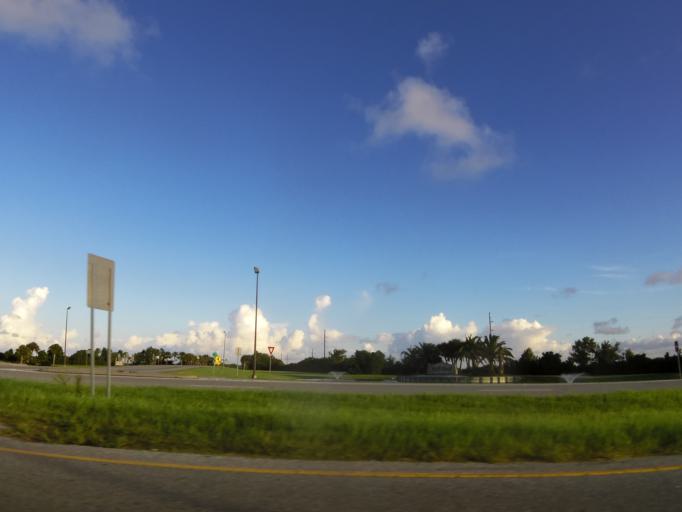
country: US
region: Georgia
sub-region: Glynn County
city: Brunswick
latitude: 31.1059
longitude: -81.4936
